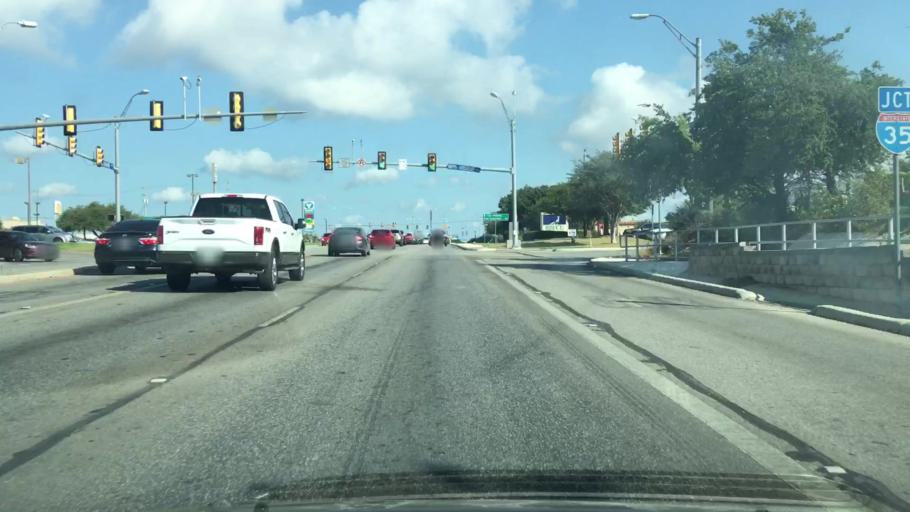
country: US
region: Texas
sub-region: Bexar County
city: Selma
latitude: 29.5974
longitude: -98.2750
